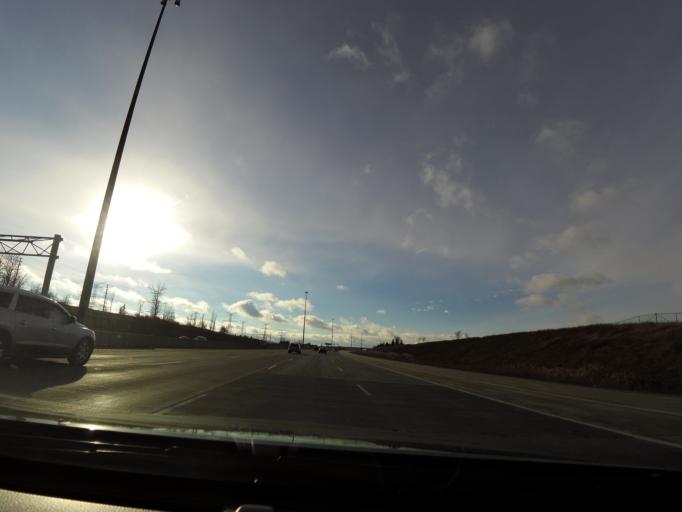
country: CA
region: Ontario
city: Brampton
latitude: 43.6158
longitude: -79.7668
